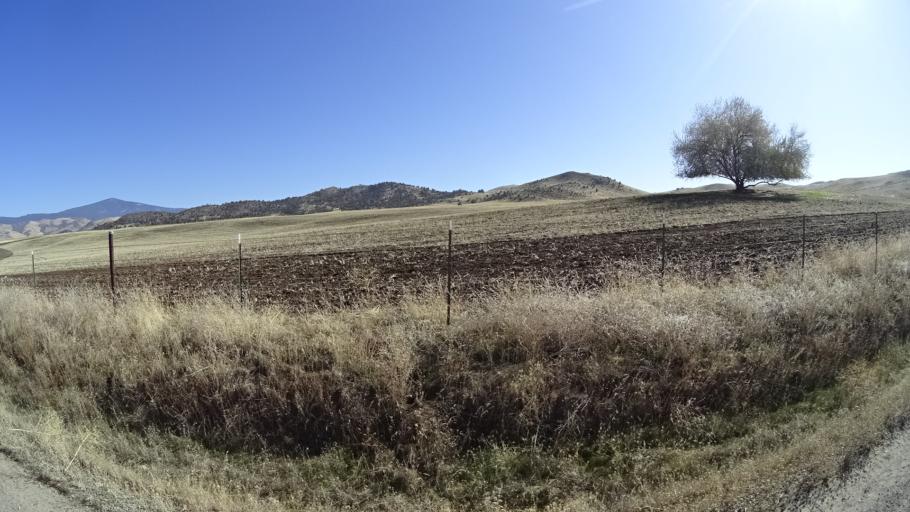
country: US
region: California
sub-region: Siskiyou County
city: Montague
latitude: 41.7971
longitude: -122.4164
